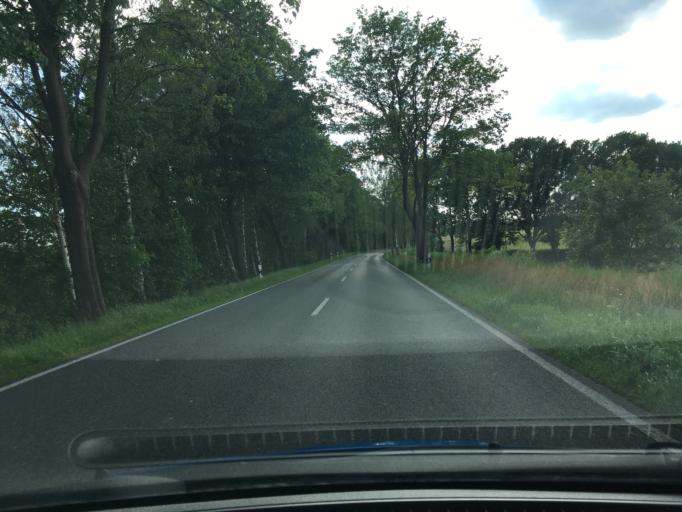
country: DE
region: Lower Saxony
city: Welle
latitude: 53.2430
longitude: 9.8204
